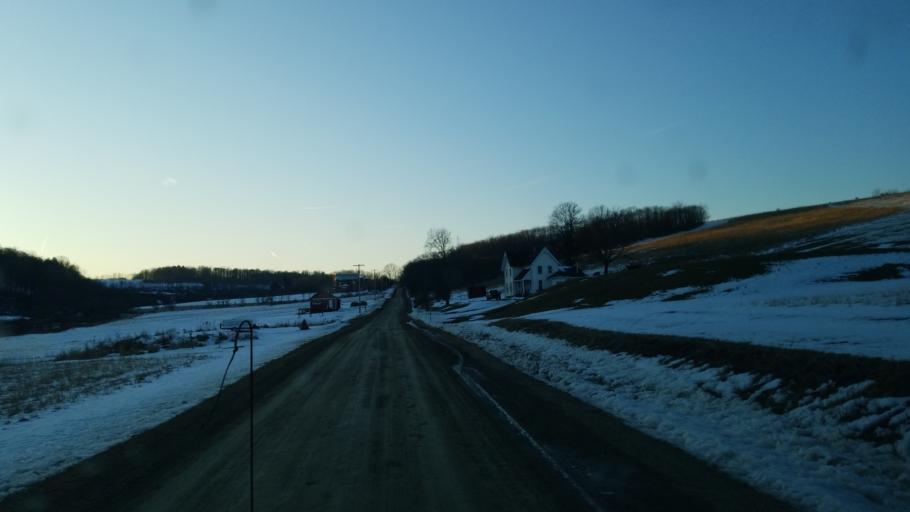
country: US
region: Pennsylvania
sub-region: Tioga County
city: Westfield
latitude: 42.0399
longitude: -77.5926
